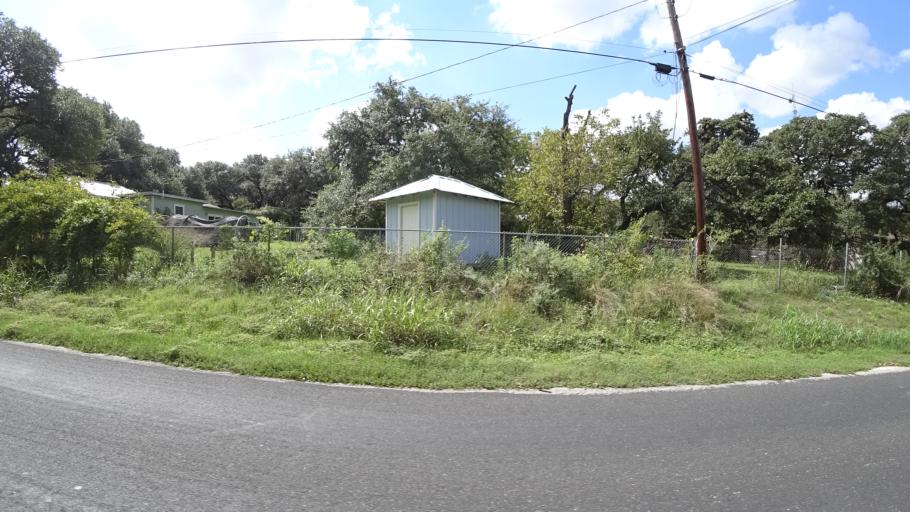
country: US
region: Texas
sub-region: Travis County
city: Onion Creek
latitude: 30.1977
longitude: -97.8026
